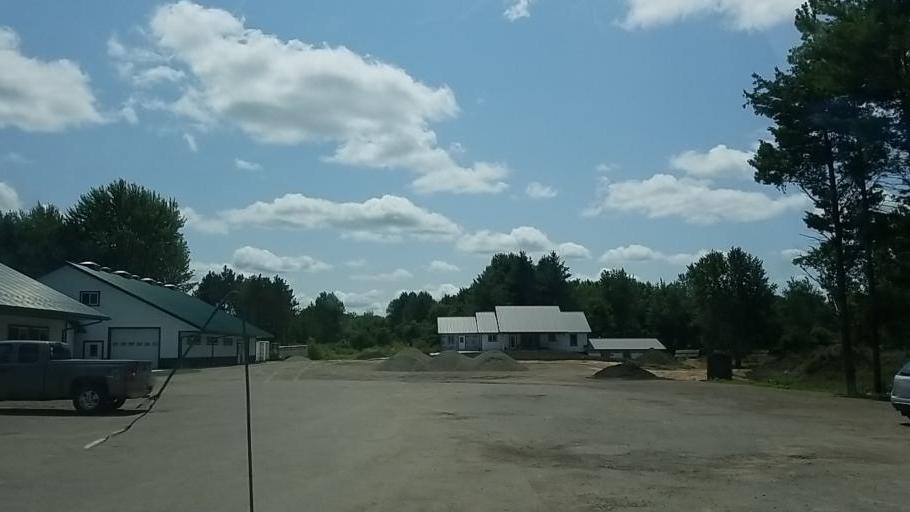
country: US
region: Michigan
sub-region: Newaygo County
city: Fremont
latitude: 43.4671
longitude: -86.0413
